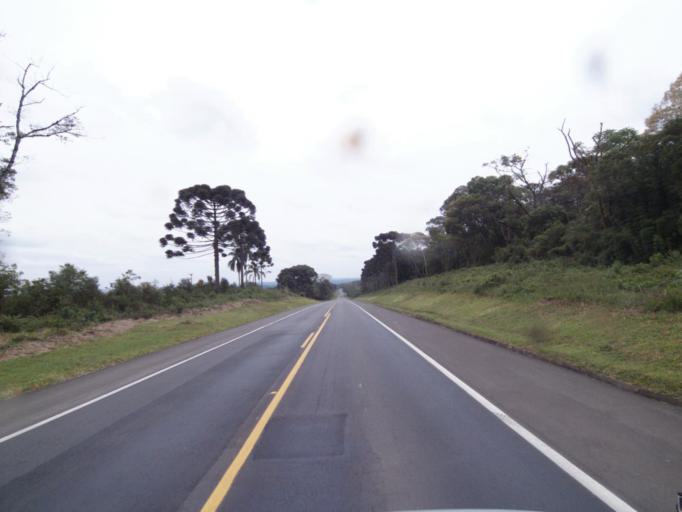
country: BR
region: Parana
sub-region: Irati
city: Irati
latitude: -25.4708
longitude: -50.4985
